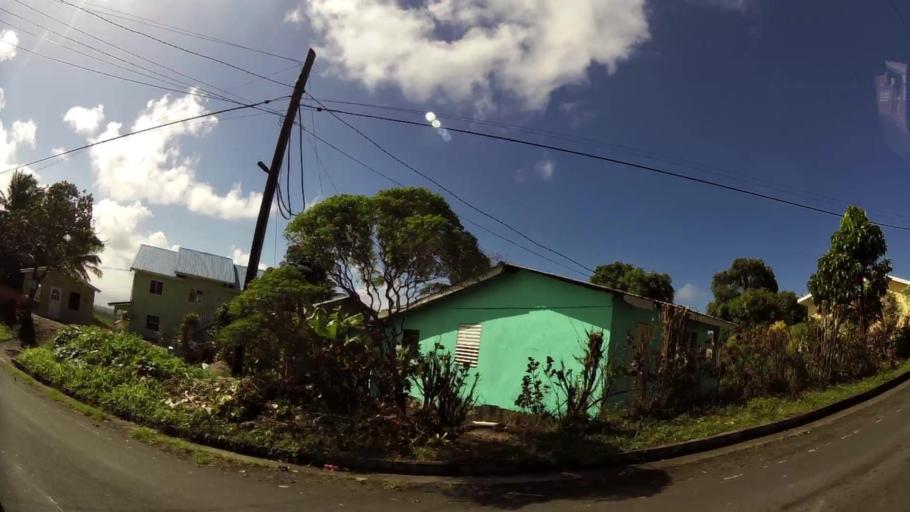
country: LC
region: Choiseul Quarter
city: Choiseul
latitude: 13.8052
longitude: -61.0366
